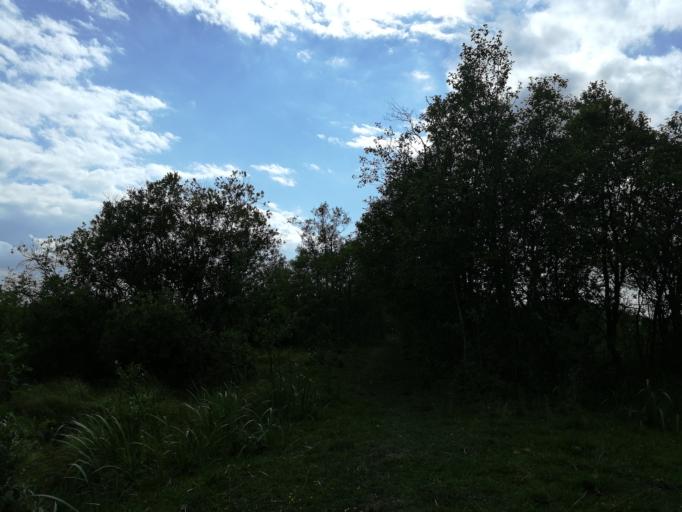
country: EE
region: Laeaene
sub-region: Lihula vald
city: Lihula
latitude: 58.7267
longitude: 23.8020
